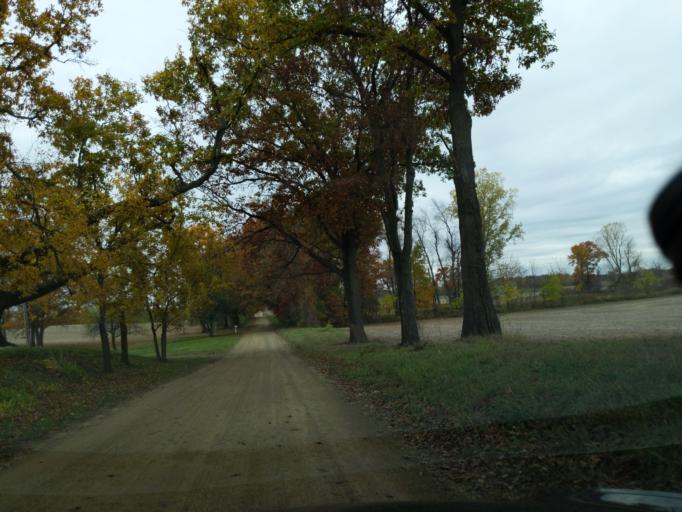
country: US
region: Michigan
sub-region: Eaton County
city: Eaton Rapids
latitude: 42.4325
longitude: -84.6005
